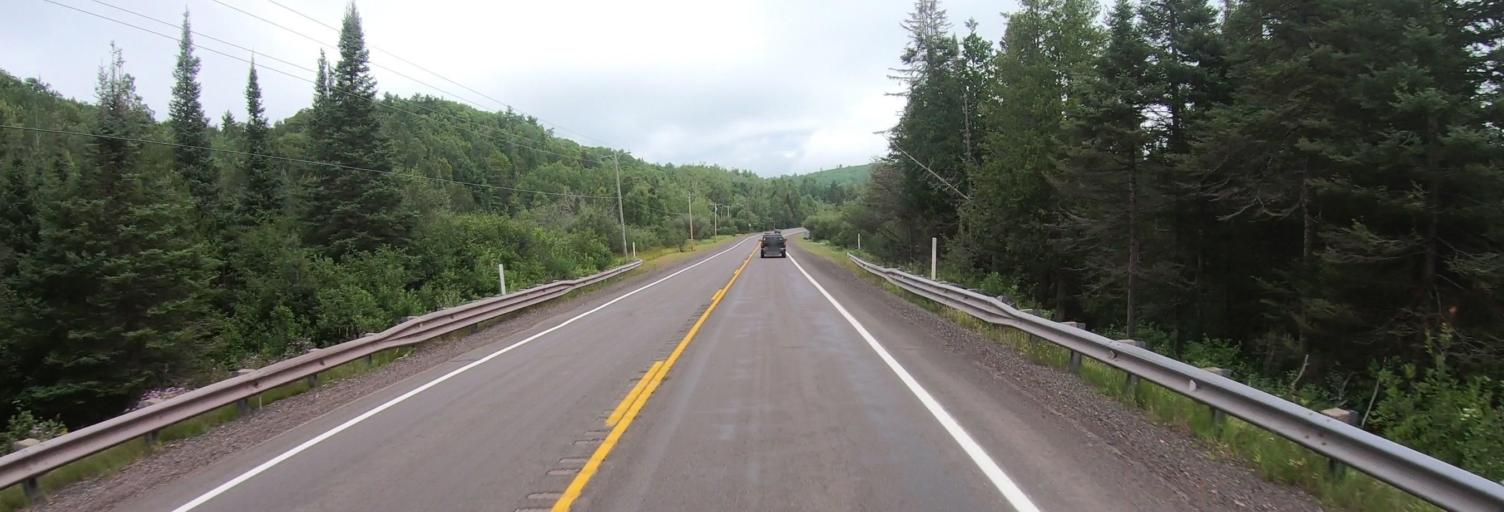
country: US
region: Michigan
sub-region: Keweenaw County
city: Eagle River
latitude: 47.3869
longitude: -88.2865
